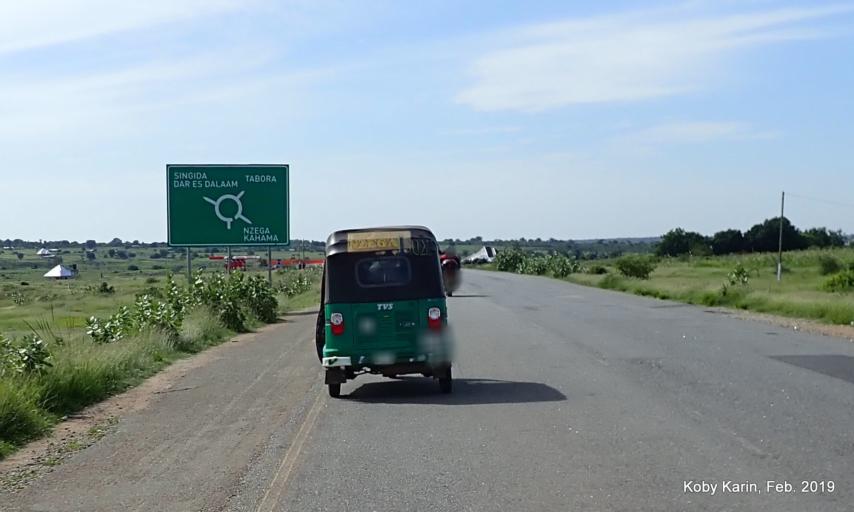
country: TZ
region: Tabora
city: Nzega
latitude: -4.2131
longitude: 33.2218
